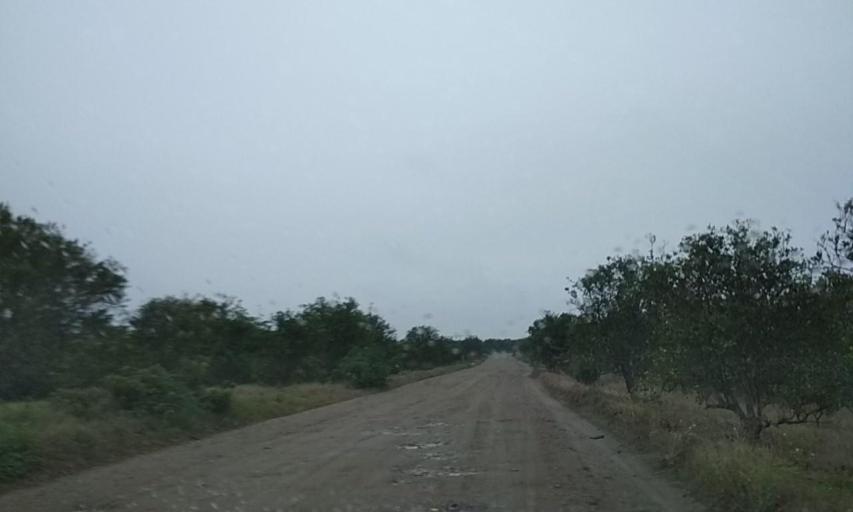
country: MX
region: Veracruz
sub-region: Papantla
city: El Chote
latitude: 20.3389
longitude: -97.3903
